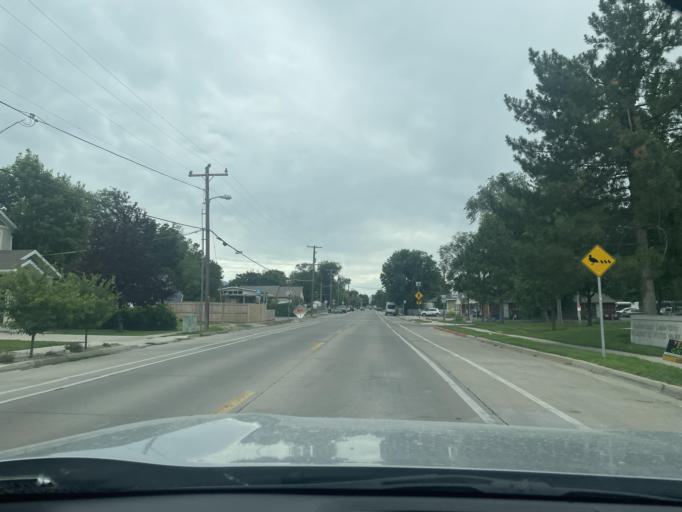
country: US
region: Utah
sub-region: Salt Lake County
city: South Salt Lake
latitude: 40.7051
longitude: -111.8769
